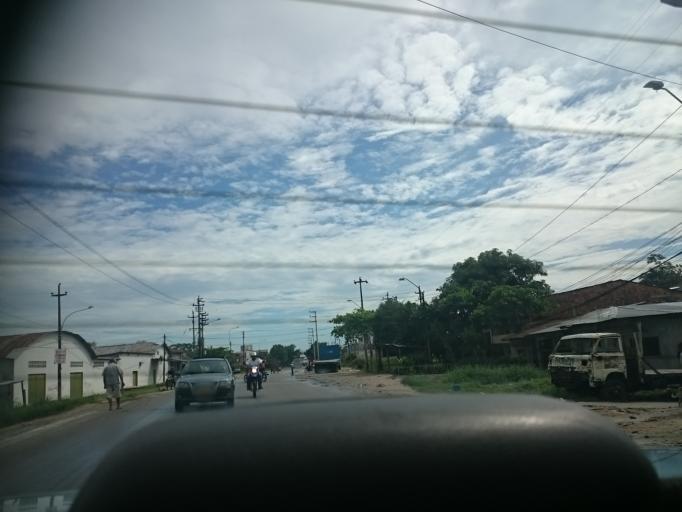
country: PE
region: Loreto
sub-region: Provincia de Maynas
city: Iquitos
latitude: -3.7887
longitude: -73.2998
